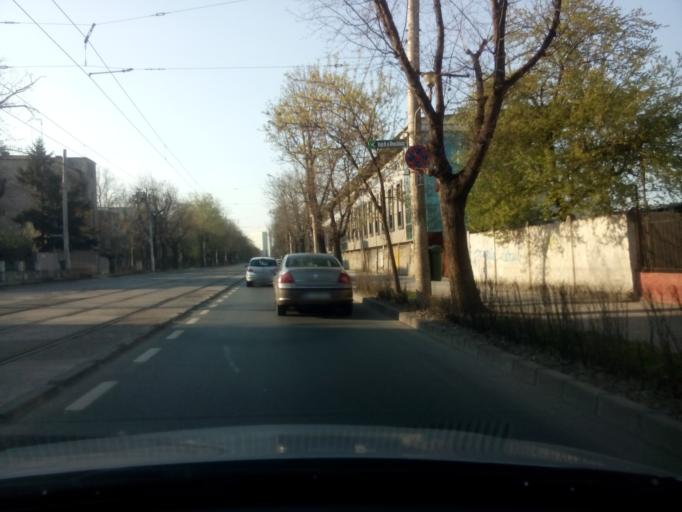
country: RO
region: Bucuresti
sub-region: Municipiul Bucuresti
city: Bucuresti
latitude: 44.4693
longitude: 26.0736
